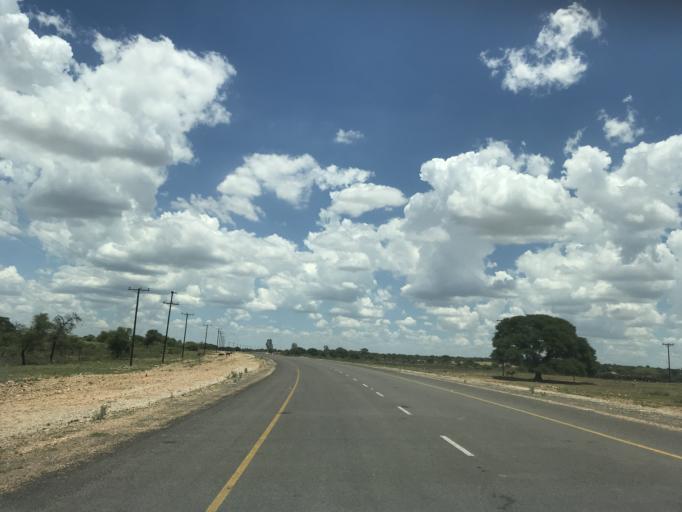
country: BW
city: Mabuli
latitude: -25.7596
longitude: 24.9499
